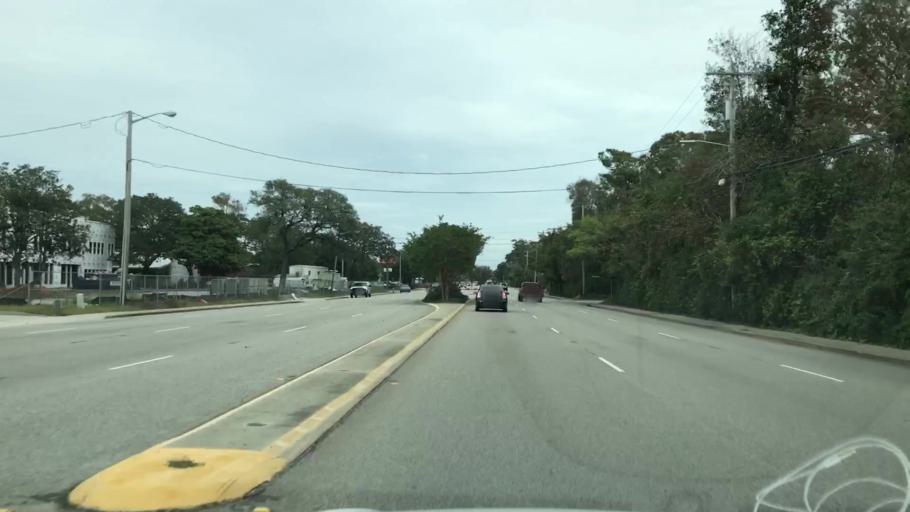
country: US
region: South Carolina
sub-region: Horry County
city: Myrtle Beach
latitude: 33.7183
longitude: -78.8529
